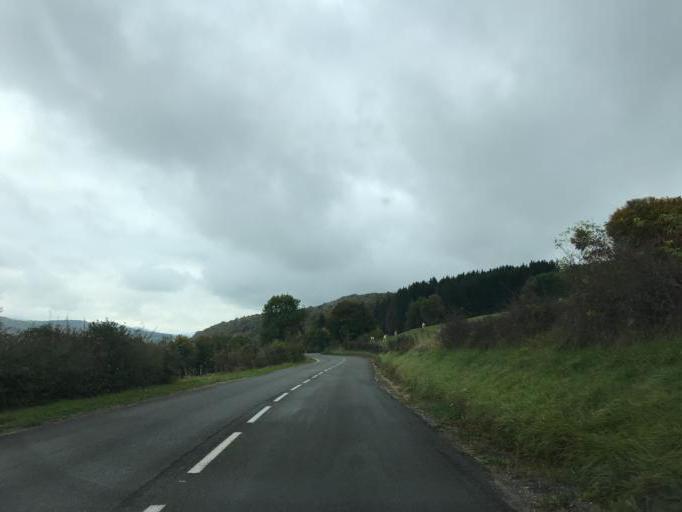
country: FR
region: Franche-Comte
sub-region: Departement du Jura
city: Orgelet
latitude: 46.4966
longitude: 5.5873
